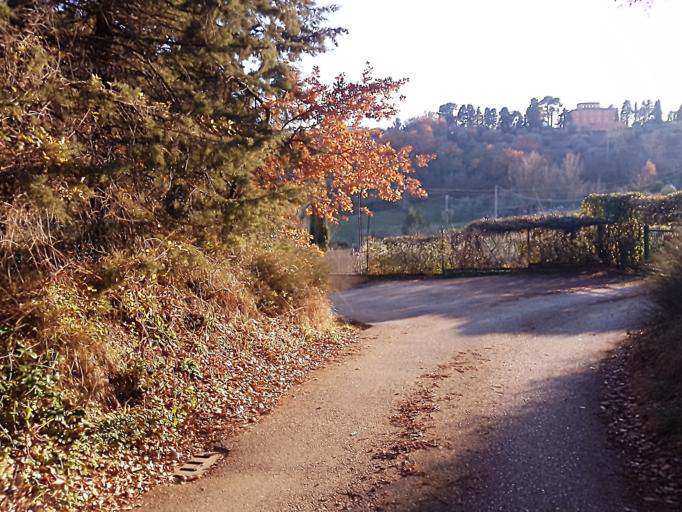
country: IT
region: Umbria
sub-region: Provincia di Perugia
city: Perugia
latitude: 43.0924
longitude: 12.3798
